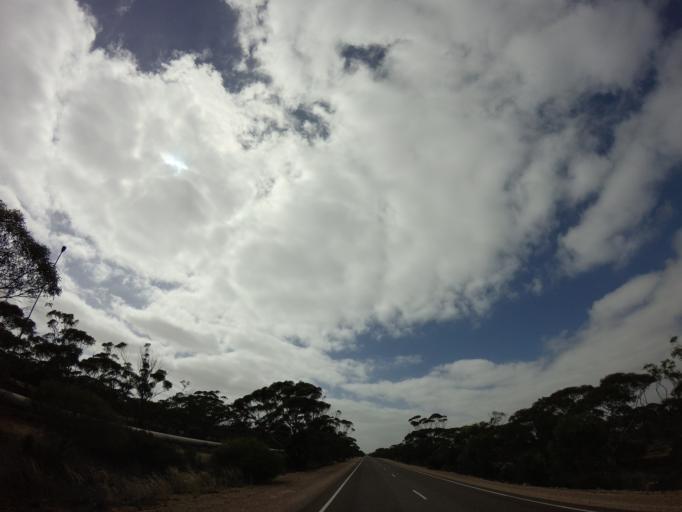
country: AU
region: South Australia
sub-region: Streaky Bay
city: Streaky Bay
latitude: -32.7047
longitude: 134.8177
